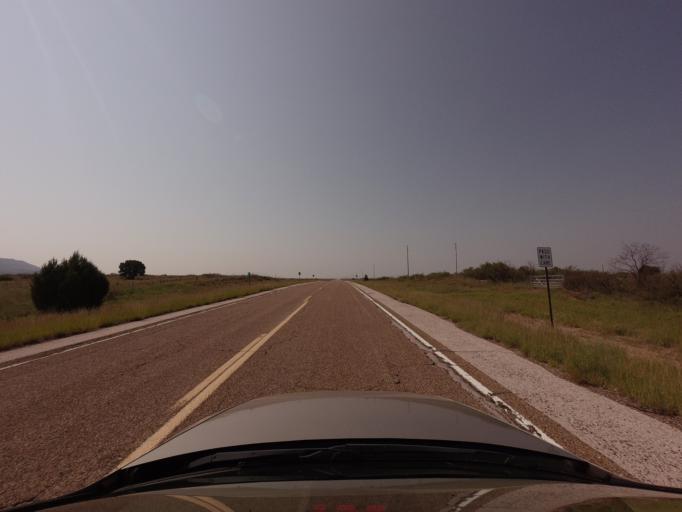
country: US
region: New Mexico
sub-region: Quay County
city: Tucumcari
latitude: 35.0097
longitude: -103.7409
